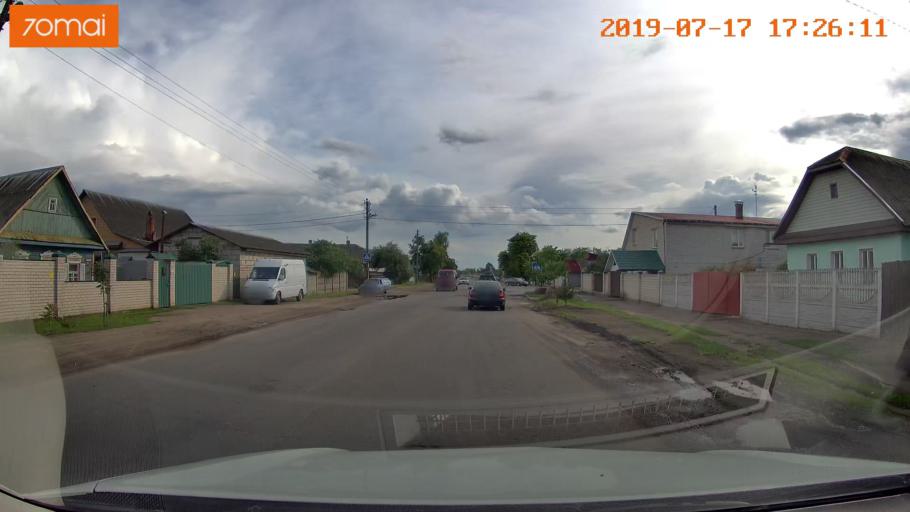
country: BY
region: Mogilev
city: Babruysk
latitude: 53.1426
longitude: 29.1730
